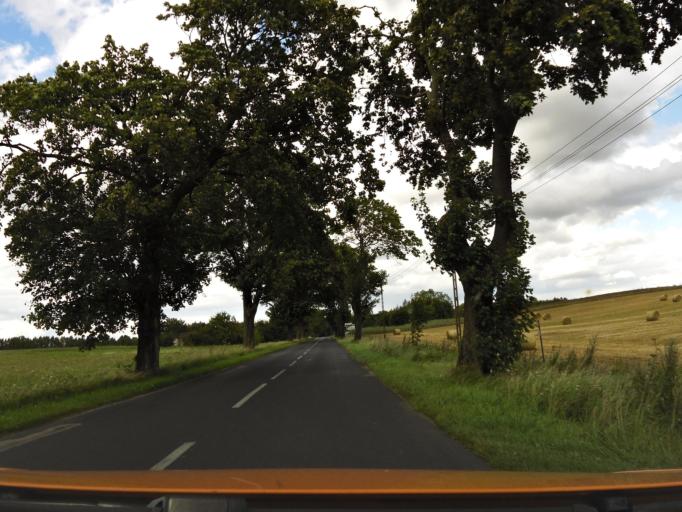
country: PL
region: West Pomeranian Voivodeship
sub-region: Powiat kolobrzeski
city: Goscino
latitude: 54.0506
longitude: 15.5470
